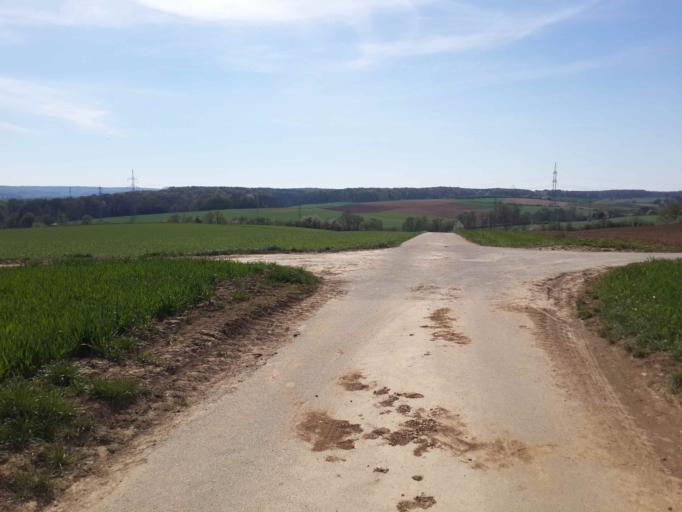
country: DE
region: Baden-Wuerttemberg
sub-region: Regierungsbezirk Stuttgart
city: Leingarten
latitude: 49.1768
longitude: 9.1359
